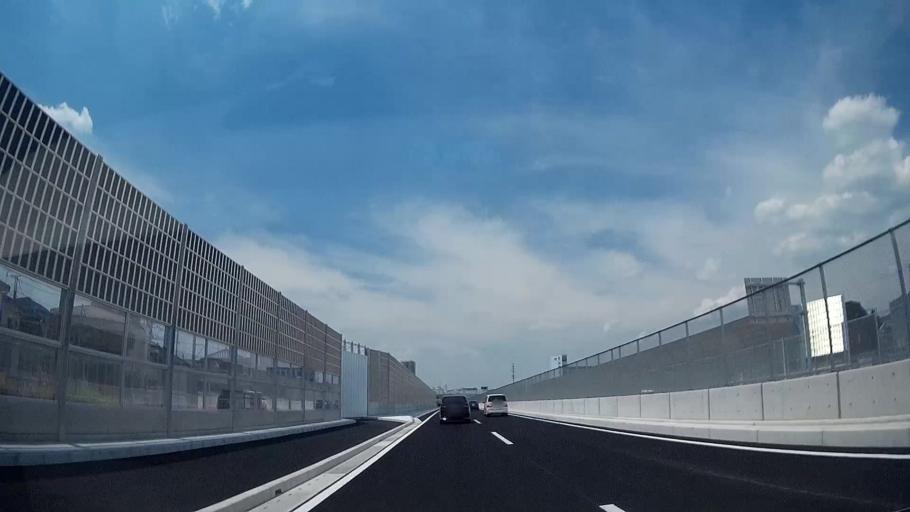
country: JP
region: Tokyo
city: Urayasu
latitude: 35.7167
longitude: 139.9188
